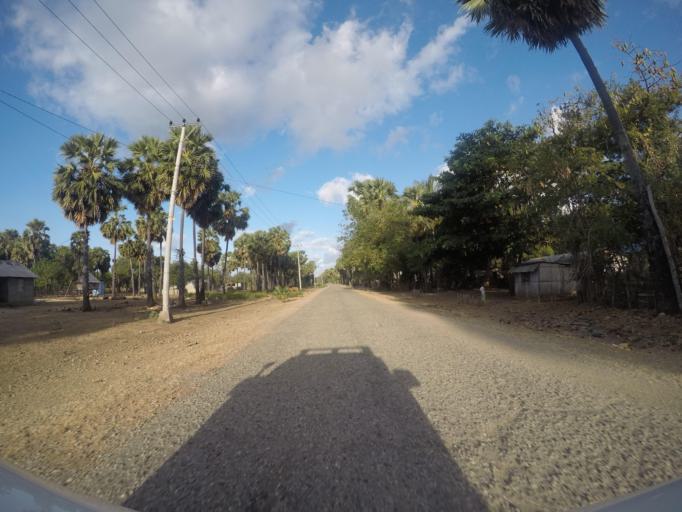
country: TL
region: Lautem
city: Lospalos
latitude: -8.3290
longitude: 126.9670
